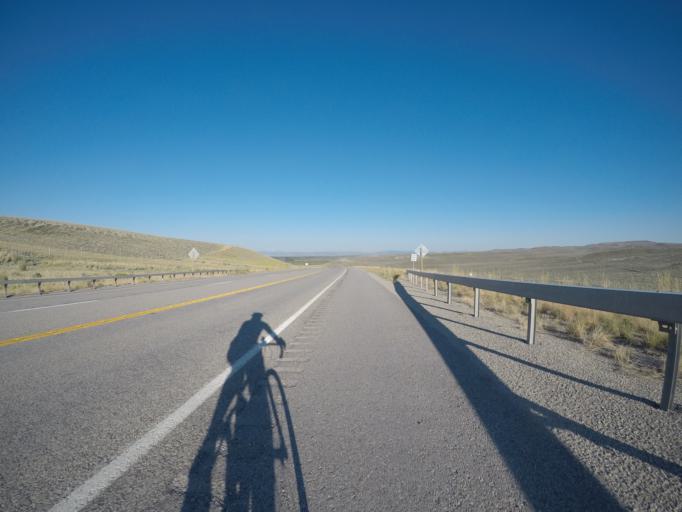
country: US
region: Wyoming
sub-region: Sublette County
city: Pinedale
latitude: 42.8821
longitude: -109.9818
